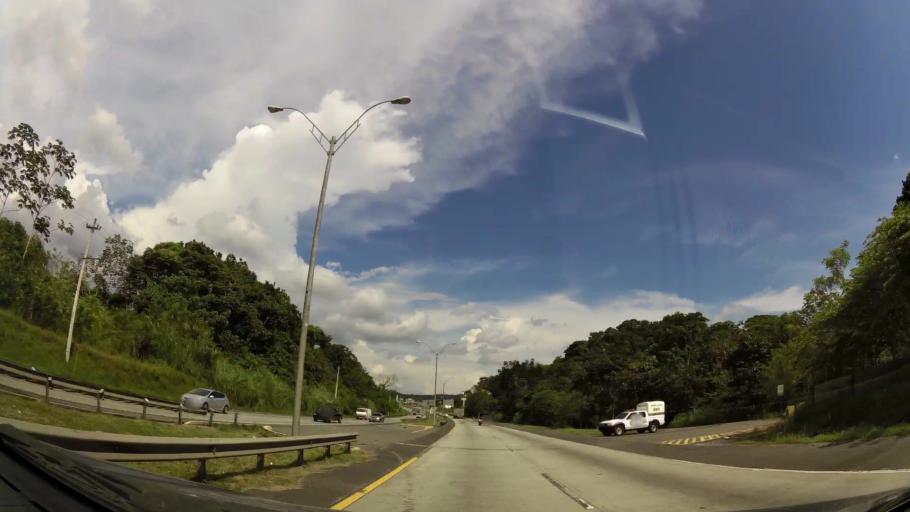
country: PA
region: Panama
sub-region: Distrito de Panama
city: Paraiso
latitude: 9.0279
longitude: -79.5914
